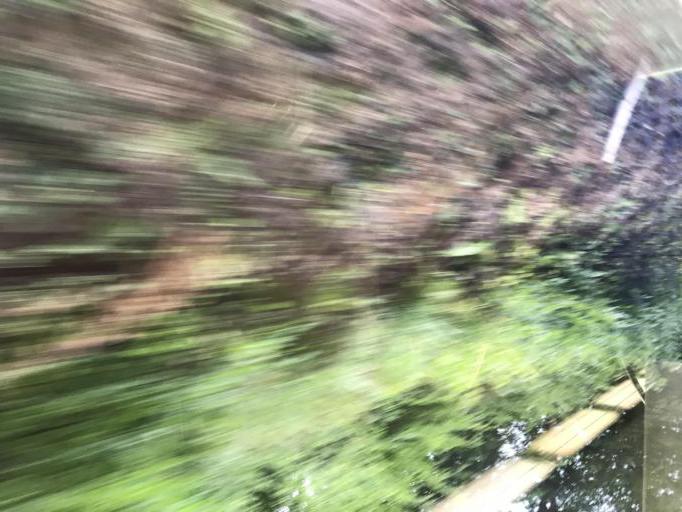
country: DE
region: Rheinland-Pfalz
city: Breitscheidt
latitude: 50.7752
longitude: 7.6386
